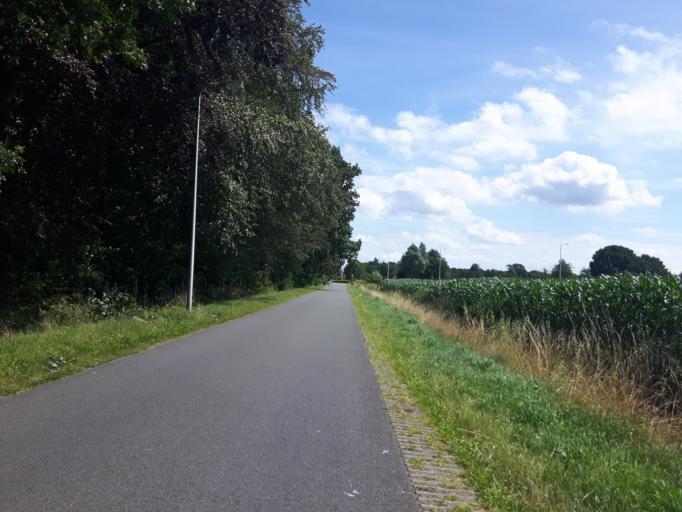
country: NL
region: Overijssel
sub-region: Gemeente Haaksbergen
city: Haaksbergen
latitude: 52.1717
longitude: 6.7555
